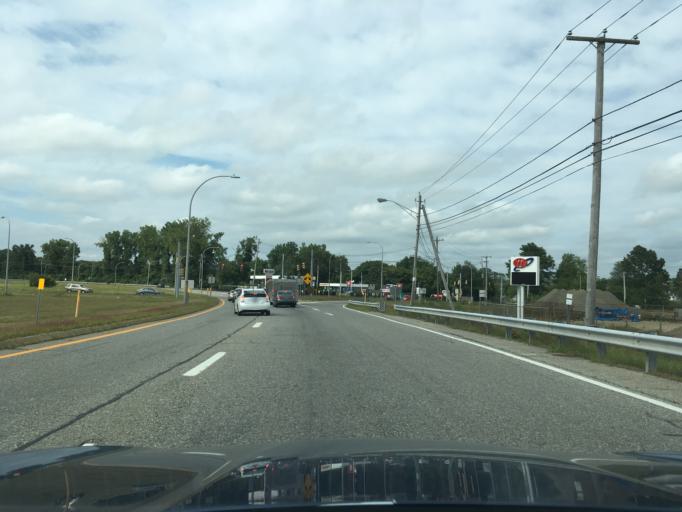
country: US
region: Massachusetts
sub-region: Bristol County
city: Seekonk
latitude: 41.7877
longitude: -71.3329
